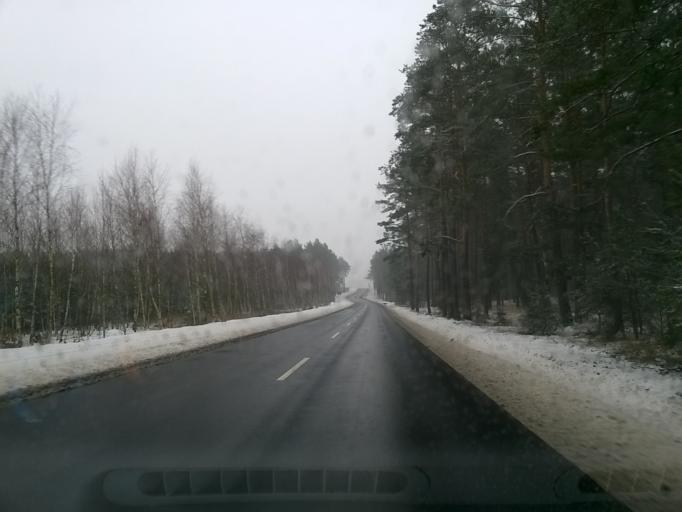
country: PL
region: Kujawsko-Pomorskie
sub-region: Powiat swiecki
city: Swiecie
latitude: 53.4227
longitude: 18.3980
